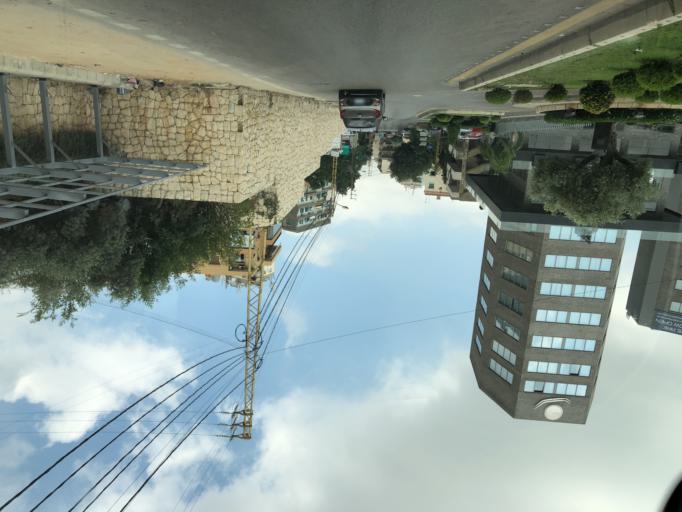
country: LB
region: Mont-Liban
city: Djounie
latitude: 33.9859
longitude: 35.6412
